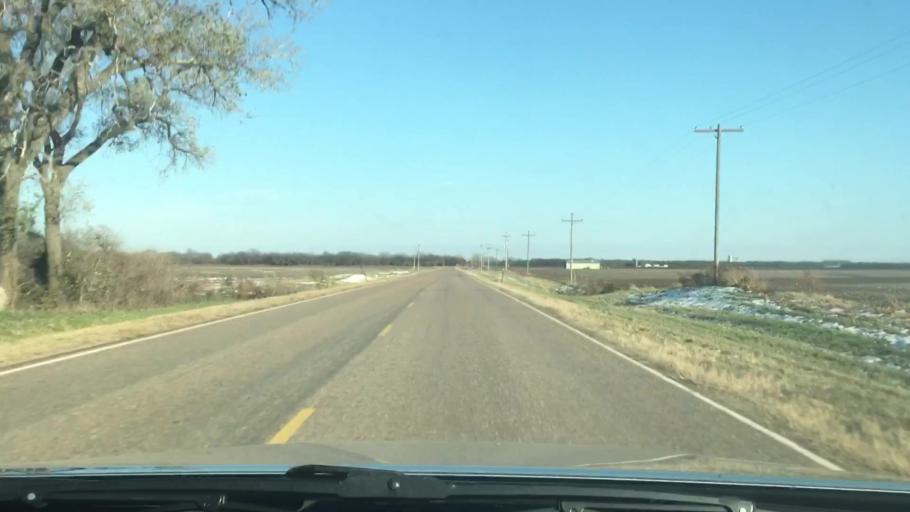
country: US
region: Kansas
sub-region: Rice County
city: Lyons
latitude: 38.2895
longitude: -98.1628
